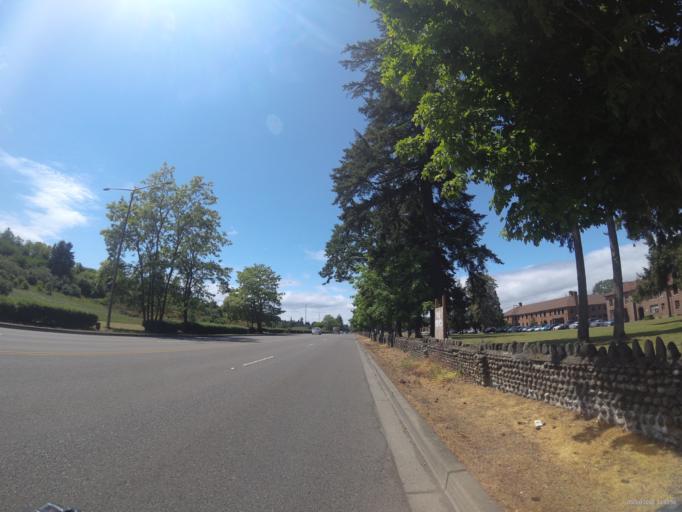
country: US
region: Washington
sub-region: Pierce County
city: Steilacoom
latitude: 47.1768
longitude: -122.5690
